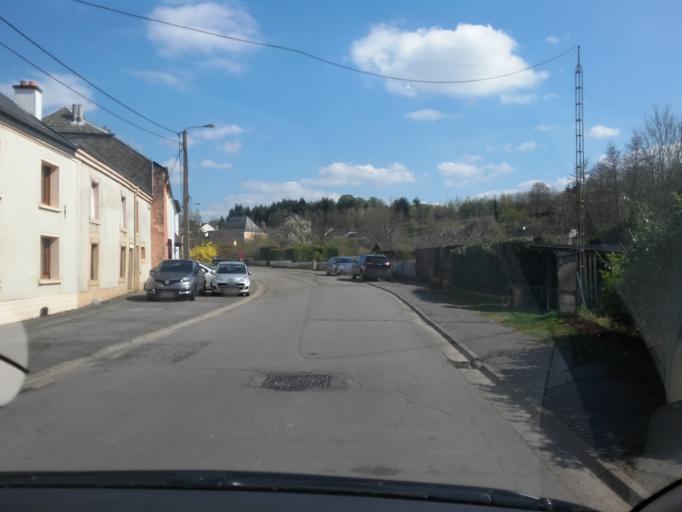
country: BE
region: Wallonia
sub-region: Province du Luxembourg
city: Habay-la-Vieille
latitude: 49.7321
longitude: 5.6505
